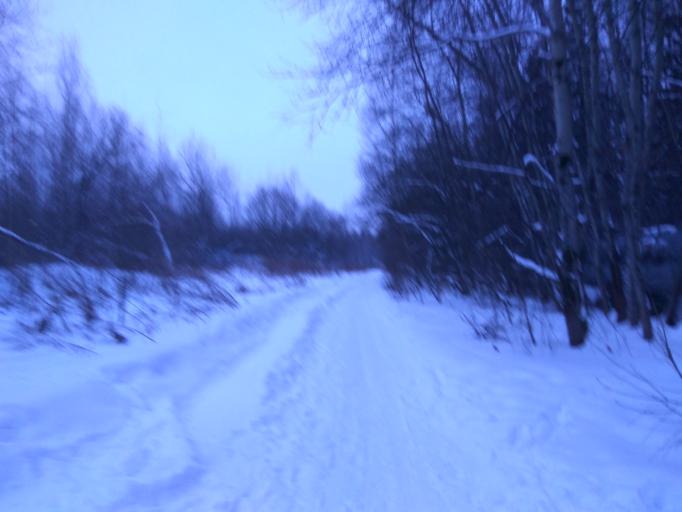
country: RU
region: Moscow
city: Biryulevo
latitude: 55.5921
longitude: 37.7008
